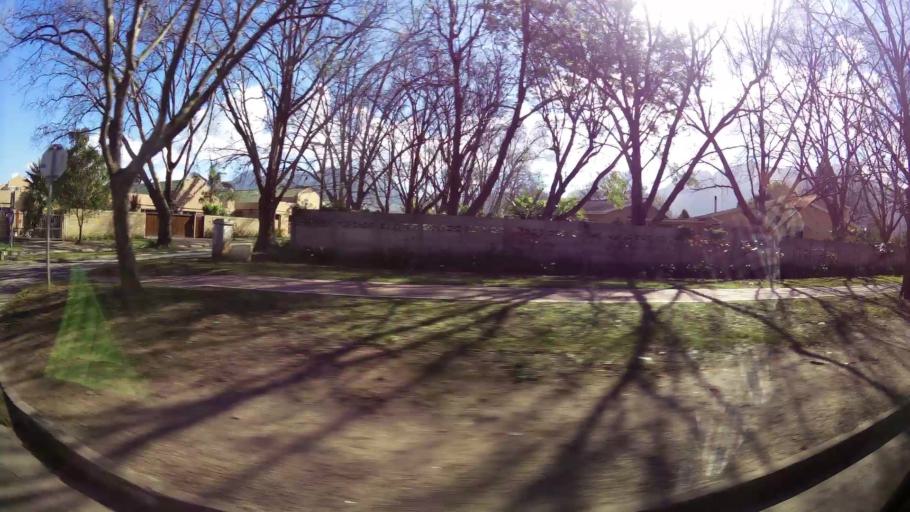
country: ZA
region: Western Cape
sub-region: Eden District Municipality
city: George
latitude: -33.9514
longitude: 22.4283
